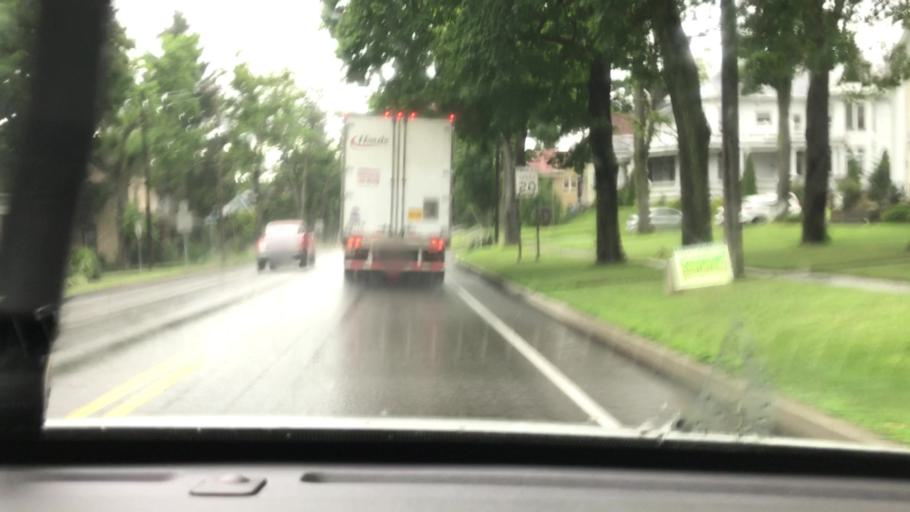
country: US
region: Pennsylvania
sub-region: Centre County
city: Philipsburg
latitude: 40.8947
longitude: -78.2189
